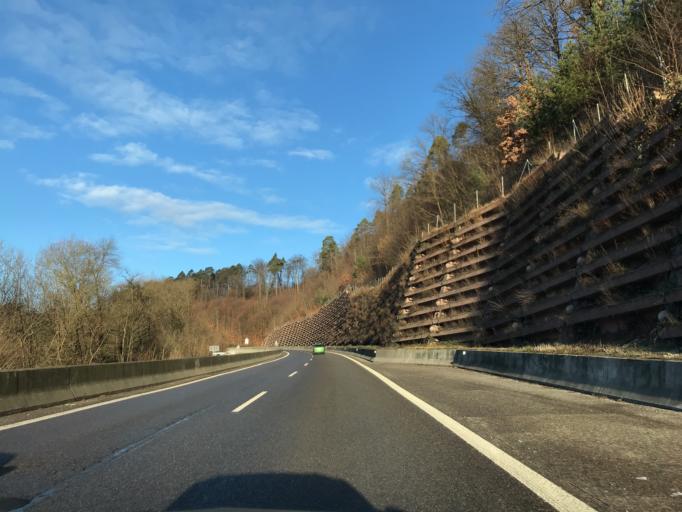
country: DE
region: Baden-Wuerttemberg
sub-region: Regierungsbezirk Stuttgart
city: Stuttgart
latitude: 48.7558
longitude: 9.1375
